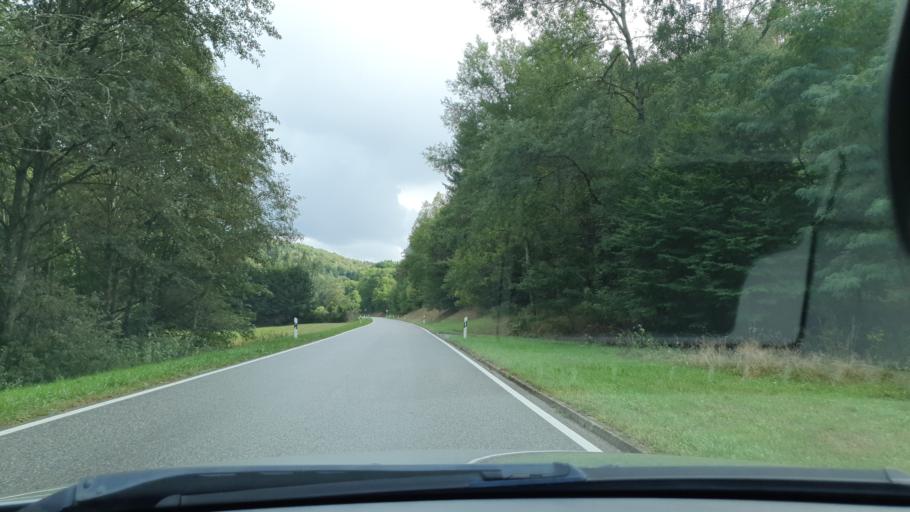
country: DE
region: Rheinland-Pfalz
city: Gerhardsbrunn
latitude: 49.3393
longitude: 7.5184
